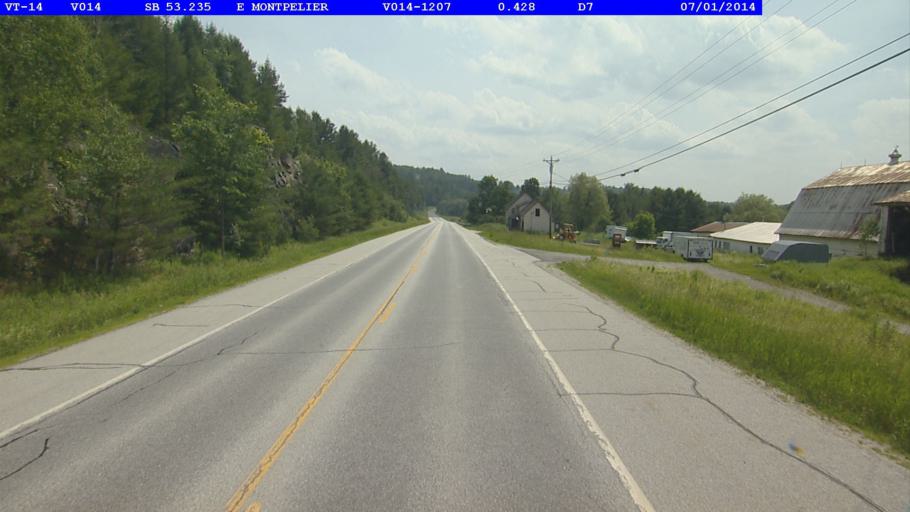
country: US
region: Vermont
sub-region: Washington County
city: Barre
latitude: 44.2415
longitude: -72.4897
